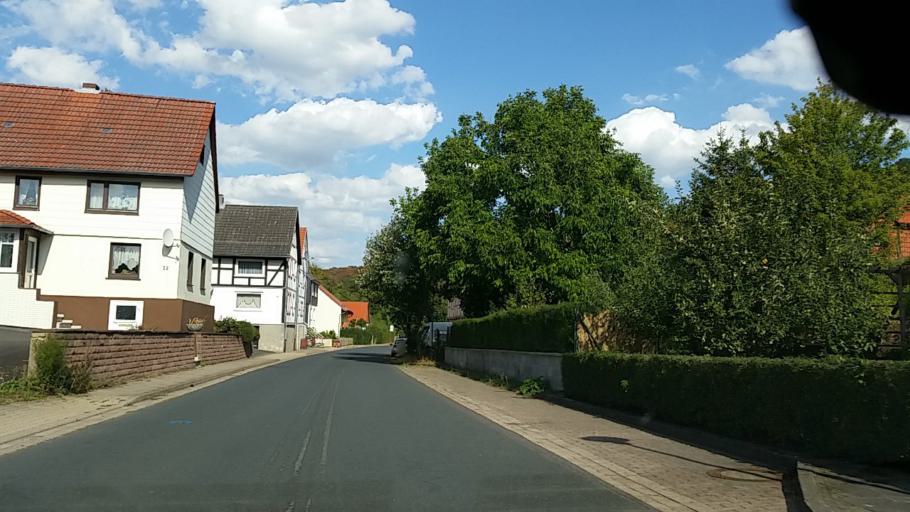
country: DE
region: Lower Saxony
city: Juhnde
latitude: 51.4265
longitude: 9.8347
